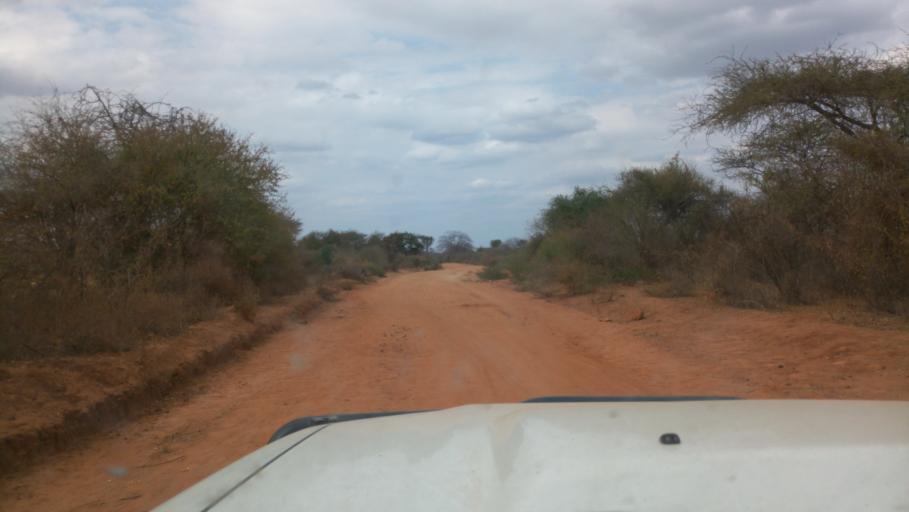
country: KE
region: Kitui
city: Kitui
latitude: -1.7986
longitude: 38.4411
